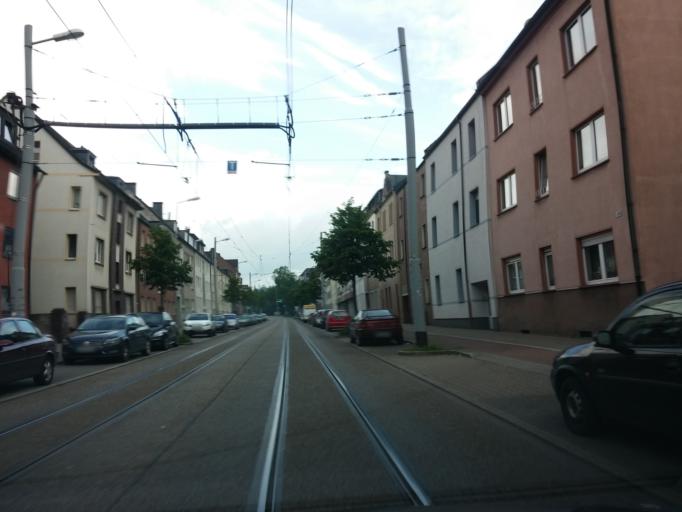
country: DE
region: North Rhine-Westphalia
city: Herten
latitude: 51.5674
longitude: 7.0815
